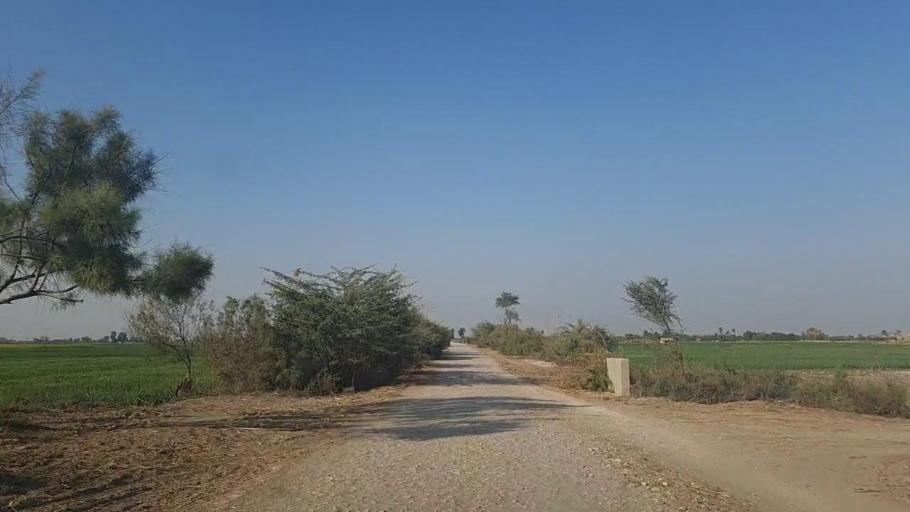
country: PK
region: Sindh
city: Jam Sahib
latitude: 26.3293
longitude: 68.7144
